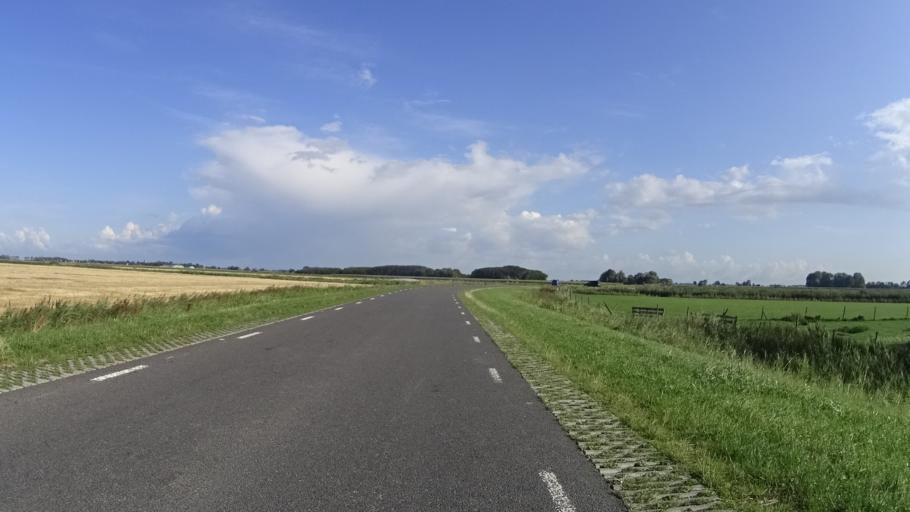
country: NL
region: Friesland
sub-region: Gemeente Harlingen
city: Harlingen
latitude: 53.1282
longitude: 5.4577
